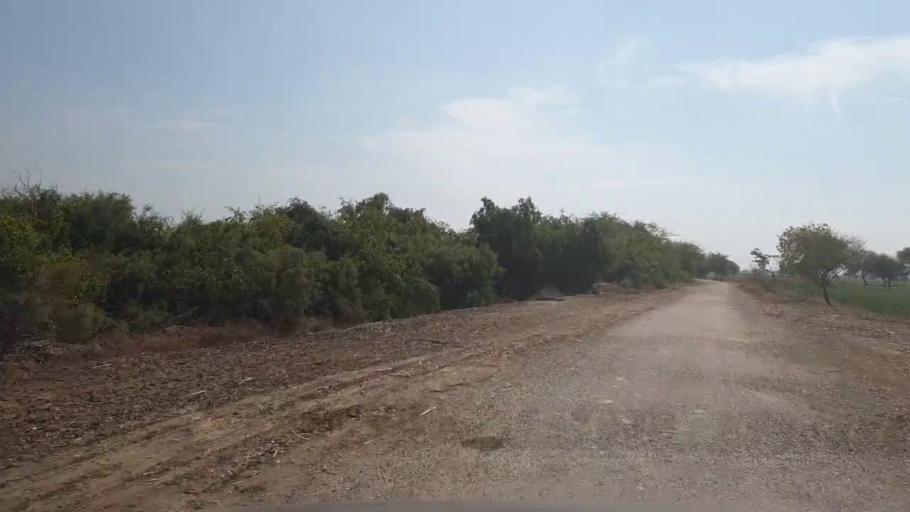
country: PK
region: Sindh
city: Mirwah Gorchani
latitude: 25.4411
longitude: 69.1926
